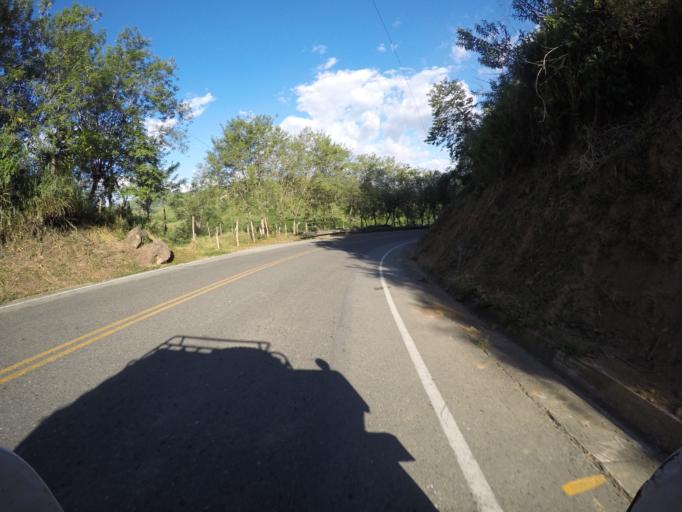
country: CO
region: Valle del Cauca
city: Cartago
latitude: 4.7125
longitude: -75.8581
